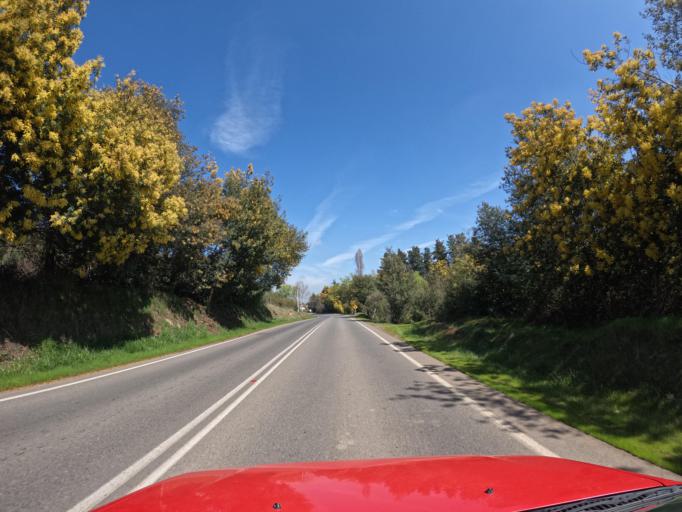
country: CL
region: Maule
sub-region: Provincia de Talca
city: San Clemente
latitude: -35.4816
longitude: -71.2704
